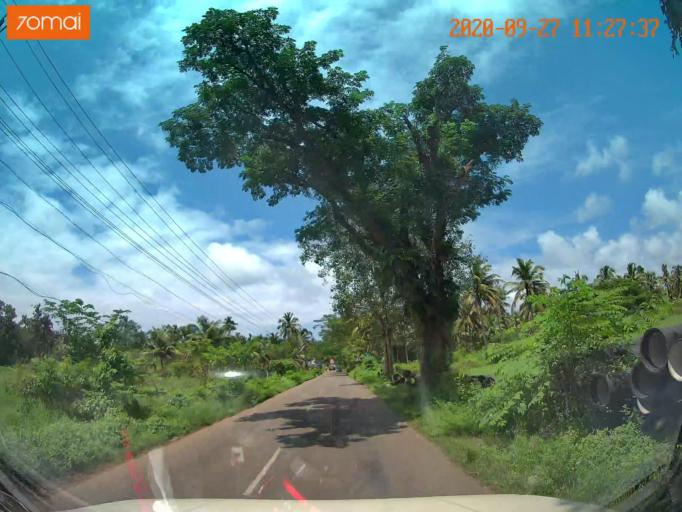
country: IN
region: Kerala
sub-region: Thrissur District
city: Thanniyam
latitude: 10.4163
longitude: 76.1453
